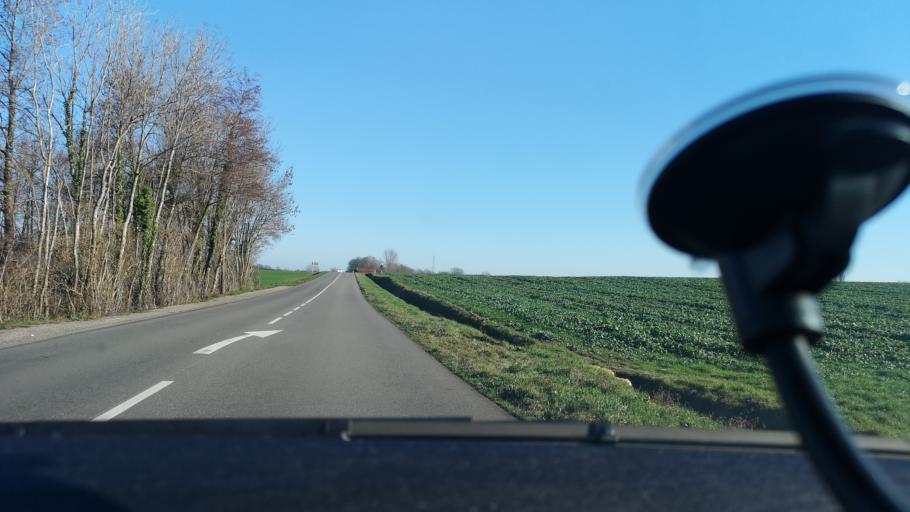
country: FR
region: Bourgogne
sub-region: Departement de Saone-et-Loire
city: Mervans
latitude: 46.7479
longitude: 5.1646
